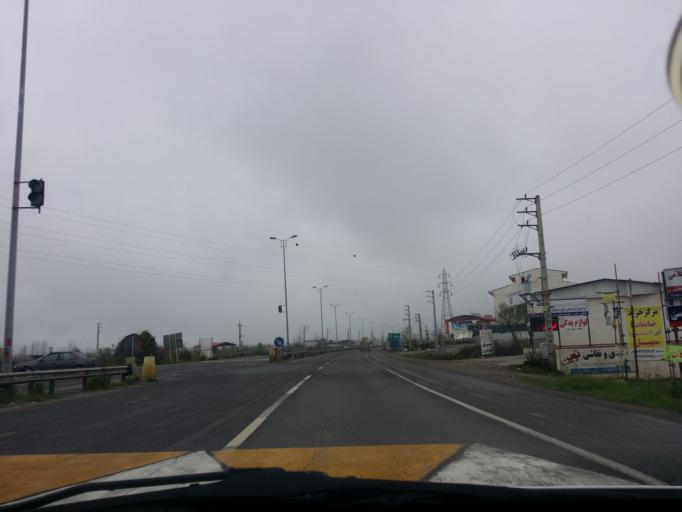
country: IR
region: Mazandaran
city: Tonekabon
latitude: 36.7966
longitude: 50.9024
